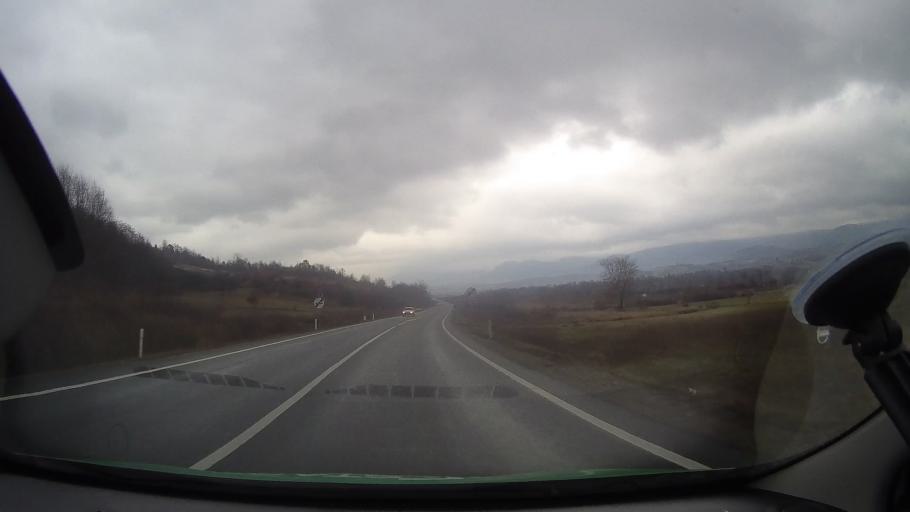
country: RO
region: Hunedoara
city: Vata de Jos
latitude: 46.2057
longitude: 22.5856
